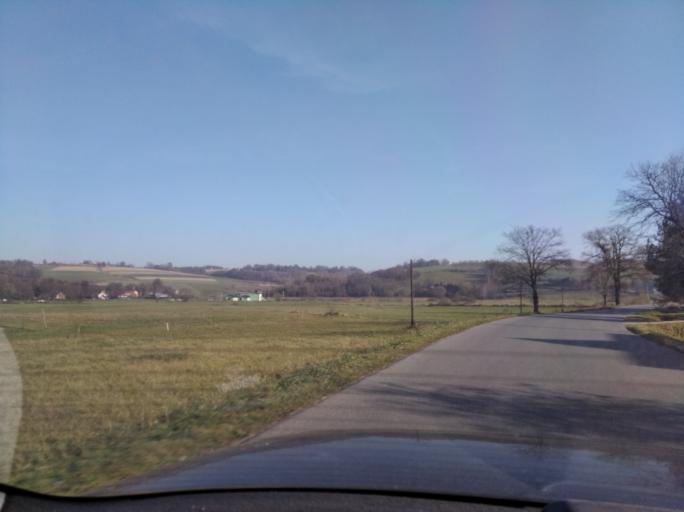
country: PL
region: Subcarpathian Voivodeship
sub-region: Powiat ropczycko-sedziszowski
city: Wielopole Skrzynskie
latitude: 49.9491
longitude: 21.5935
